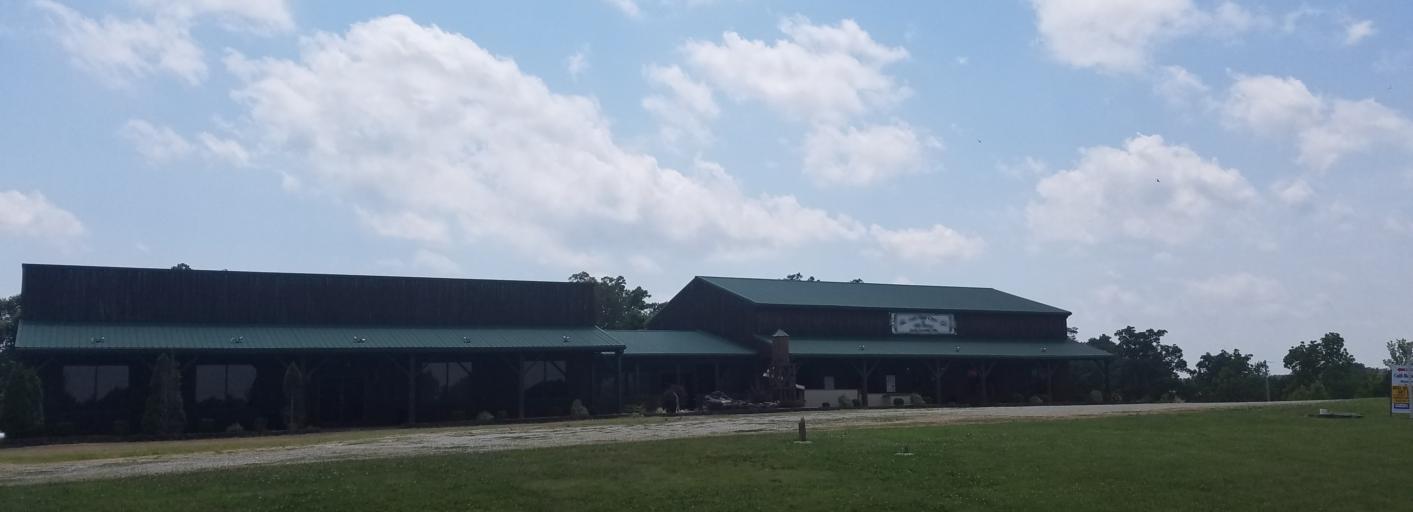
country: US
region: Kentucky
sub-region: Hart County
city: Munfordville
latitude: 37.3182
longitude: -86.0917
